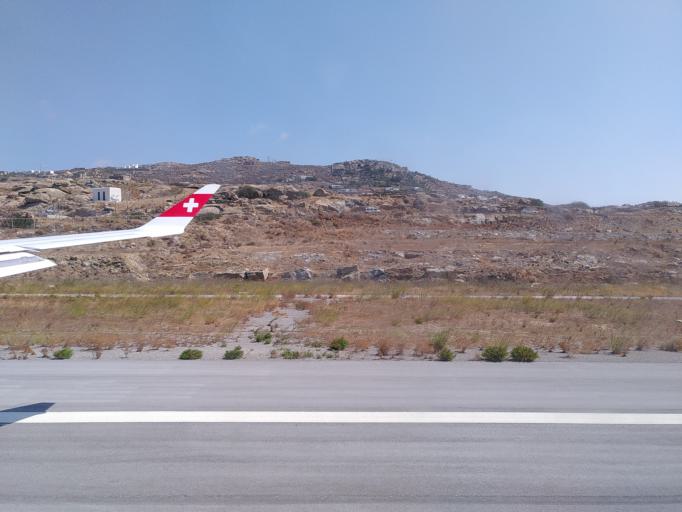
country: GR
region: South Aegean
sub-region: Nomos Kykladon
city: Mykonos
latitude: 37.4291
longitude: 25.3510
